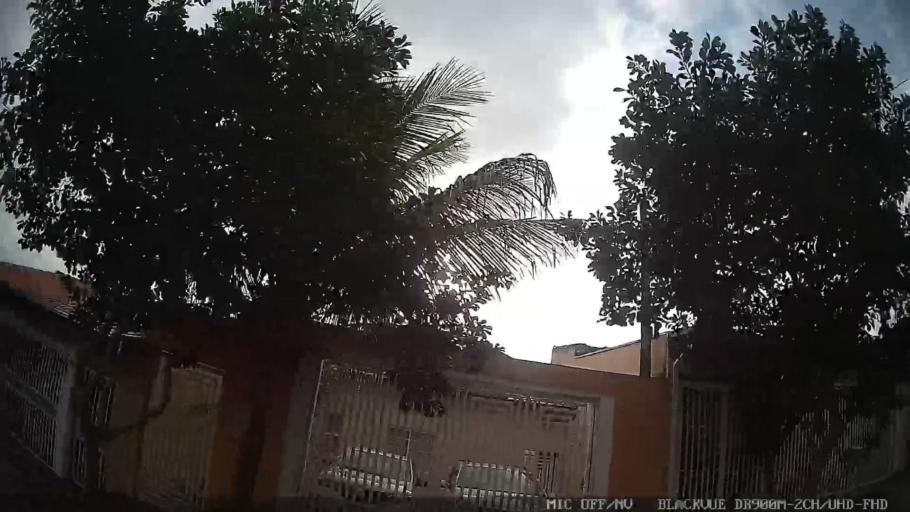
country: BR
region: Sao Paulo
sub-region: Indaiatuba
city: Indaiatuba
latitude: -23.1006
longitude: -47.2420
